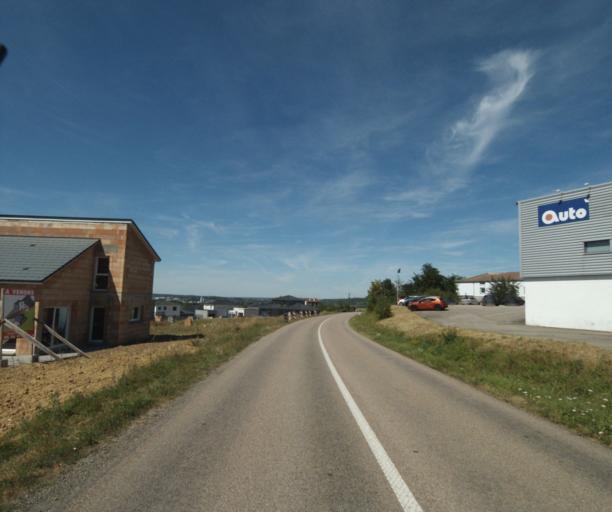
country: FR
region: Lorraine
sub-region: Departement des Vosges
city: Golbey
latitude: 48.2004
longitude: 6.4509
